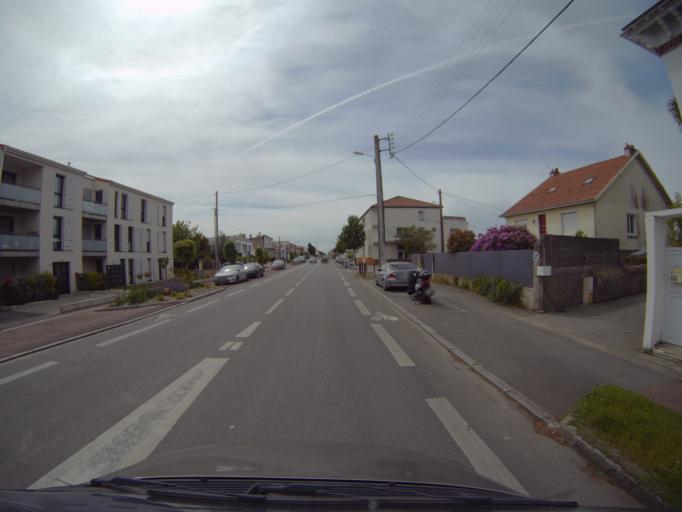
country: FR
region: Pays de la Loire
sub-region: Departement de la Loire-Atlantique
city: Reze
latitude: 47.1728
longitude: -1.5436
